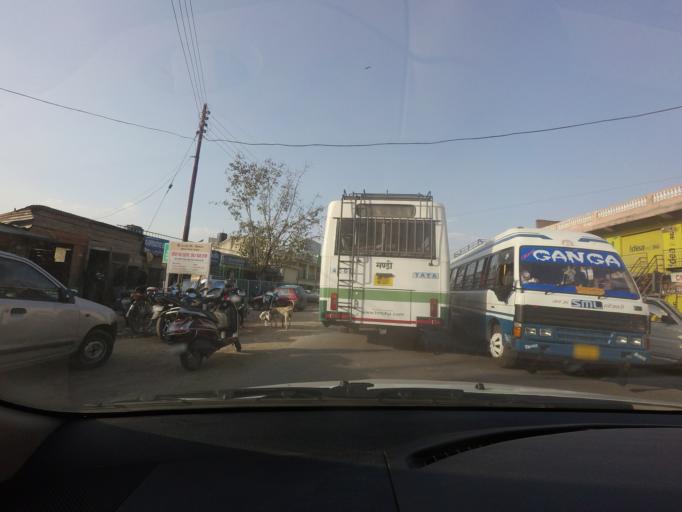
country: IN
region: Himachal Pradesh
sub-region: Mandi
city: Sundarnagar
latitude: 31.5517
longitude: 76.8994
